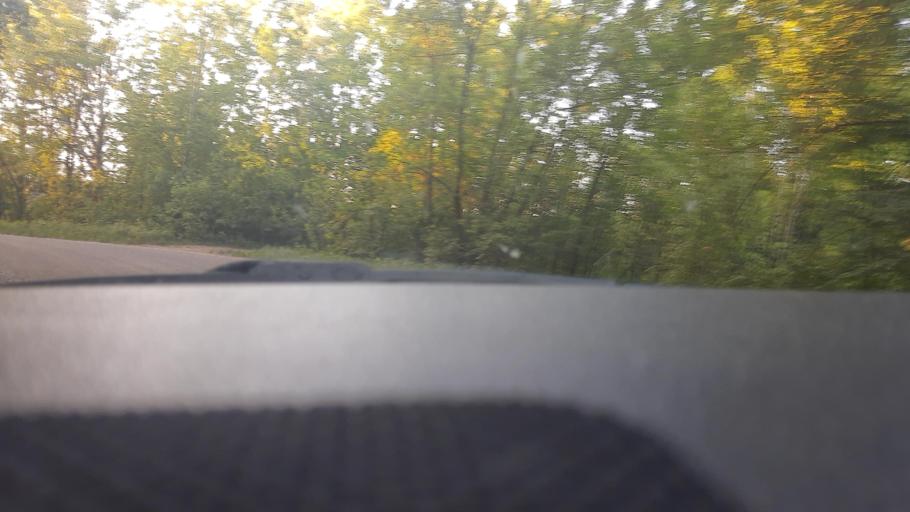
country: RU
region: Bashkortostan
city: Avdon
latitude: 54.6333
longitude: 55.5437
